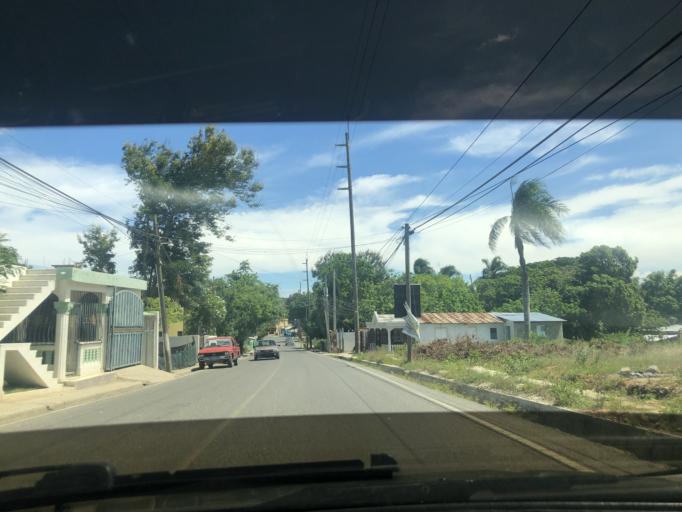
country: DO
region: Santiago
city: Santiago de los Caballeros
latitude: 19.4049
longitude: -70.6706
